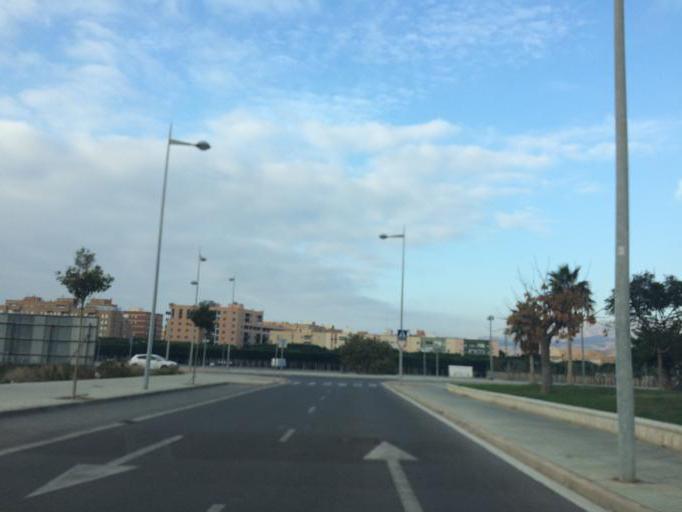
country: ES
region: Andalusia
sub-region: Provincia de Almeria
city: Almeria
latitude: 36.8295
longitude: -2.4429
